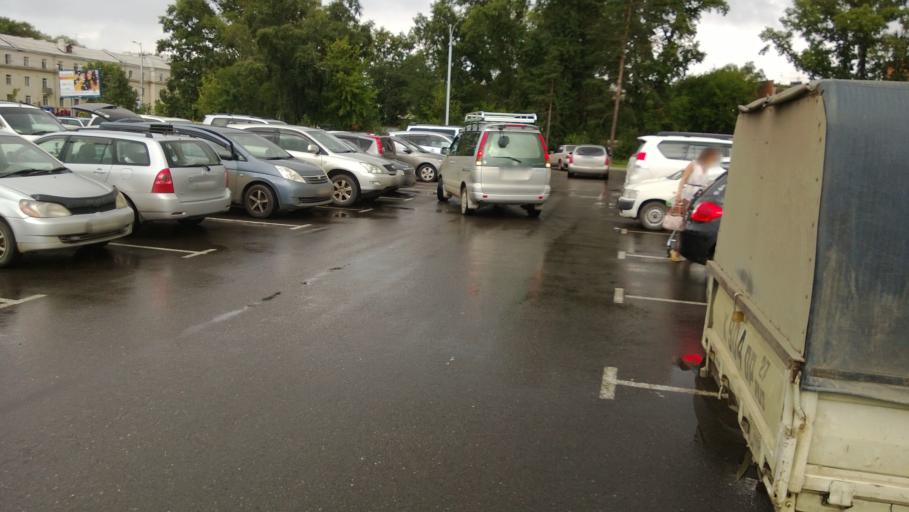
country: RU
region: Khabarovsk Krai
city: Khabarovsk Vtoroy
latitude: 48.3959
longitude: 135.1050
